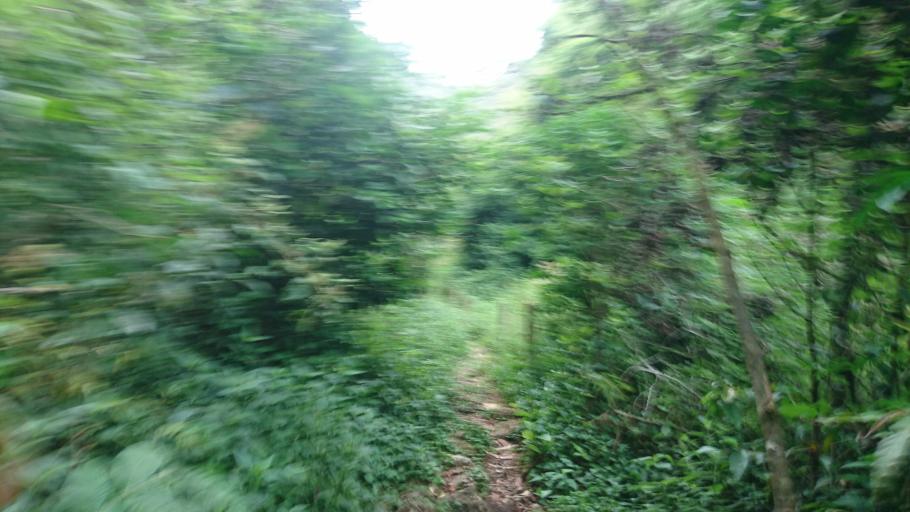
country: GT
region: Huehuetenango
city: Union
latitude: 16.1344
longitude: -91.7274
